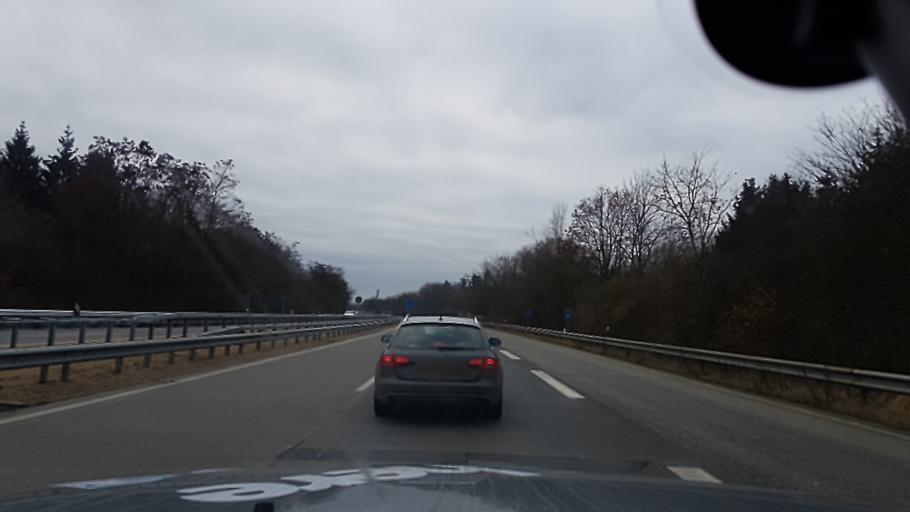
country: DE
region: Schleswig-Holstein
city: Ratekau
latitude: 53.9287
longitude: 10.7276
